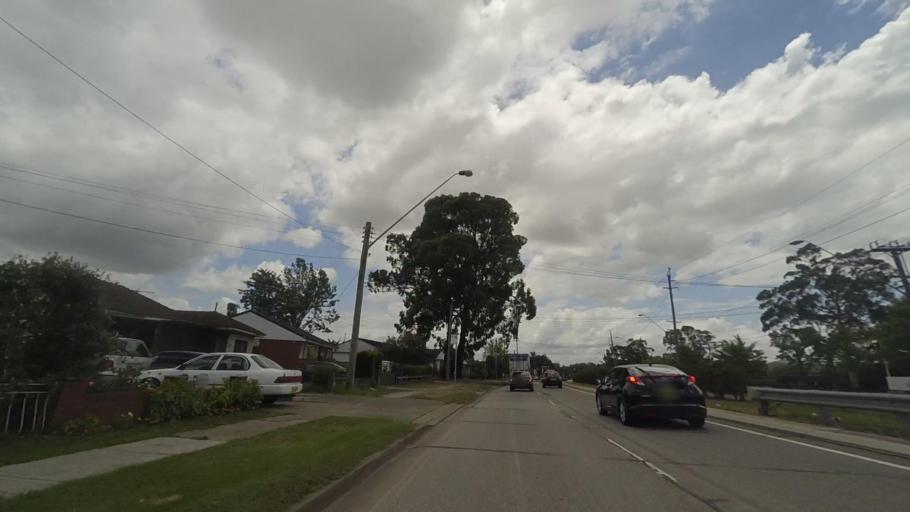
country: AU
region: New South Wales
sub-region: Fairfield
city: Cabramatta West
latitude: -33.9117
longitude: 150.9190
